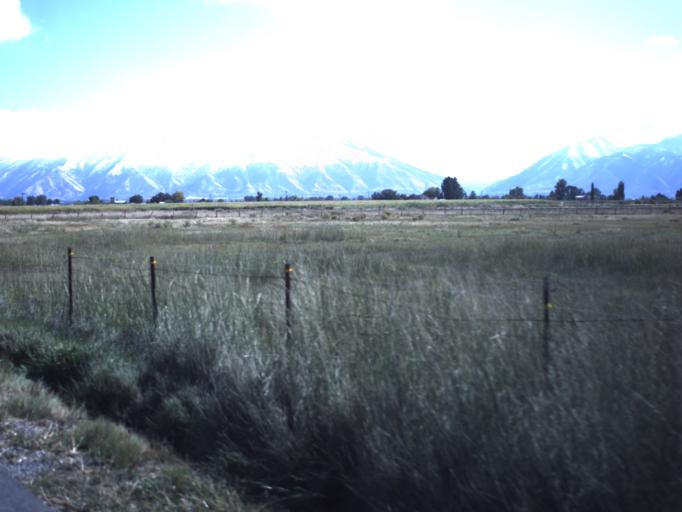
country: US
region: Utah
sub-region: Utah County
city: Benjamin
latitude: 40.1508
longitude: -111.7241
